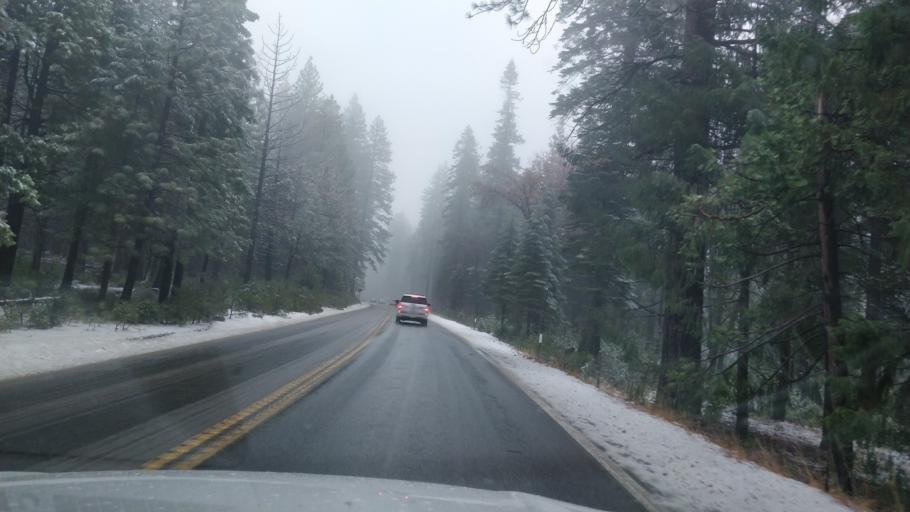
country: US
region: California
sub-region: Sierra County
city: Downieville
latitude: 39.3083
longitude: -120.7617
